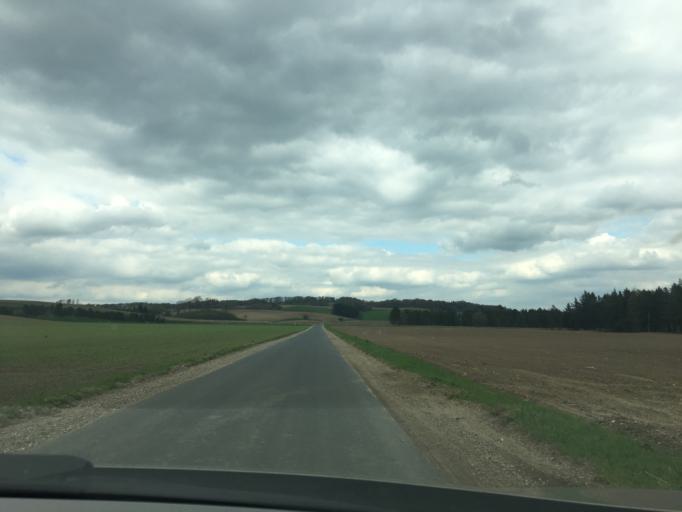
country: DK
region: Central Jutland
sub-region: Horsens Kommune
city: Braedstrup
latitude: 55.9532
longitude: 9.6660
